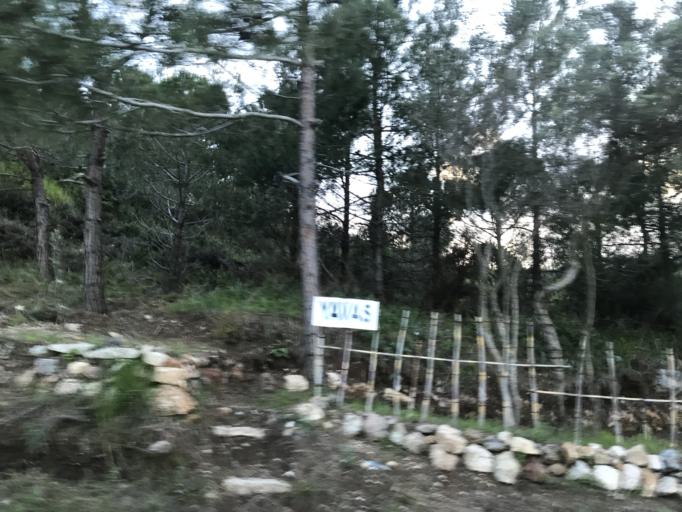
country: TR
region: Hatay
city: Uzunbag
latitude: 36.1069
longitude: 36.0431
